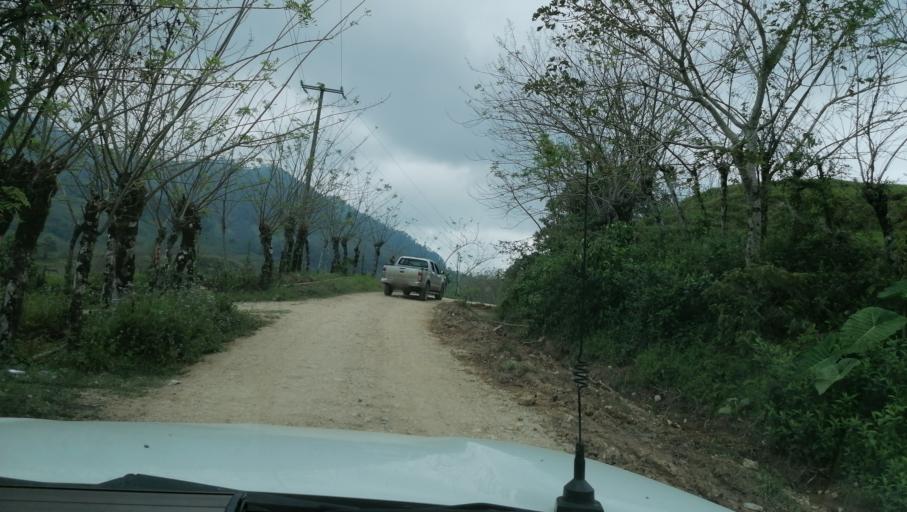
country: MX
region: Chiapas
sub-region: Ocotepec
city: San Pablo Huacano
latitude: 17.2678
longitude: -93.2551
